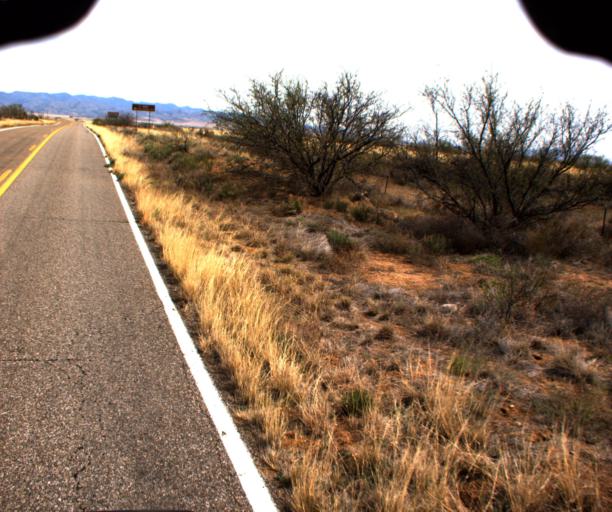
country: US
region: Arizona
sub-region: Cochise County
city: Willcox
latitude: 32.0955
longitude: -109.5364
